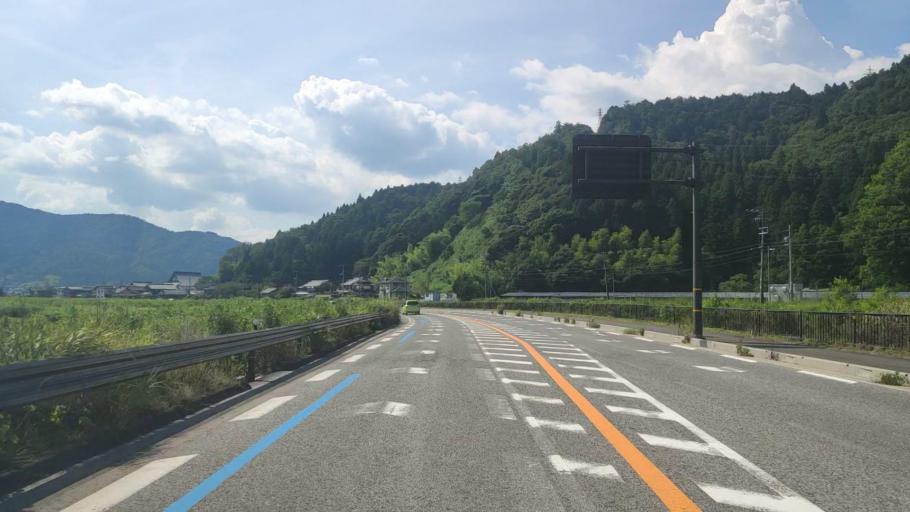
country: JP
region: Shiga Prefecture
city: Nagahama
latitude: 35.5141
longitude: 136.1719
